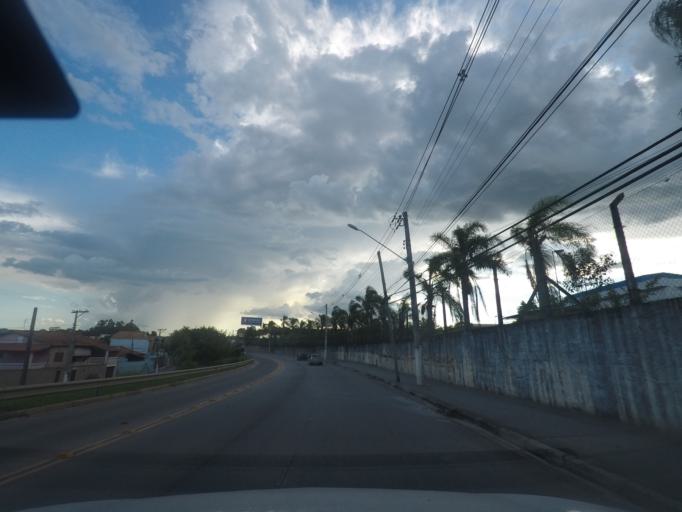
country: BR
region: Sao Paulo
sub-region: Cacapava
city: Cacapava
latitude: -23.1184
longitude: -45.7112
